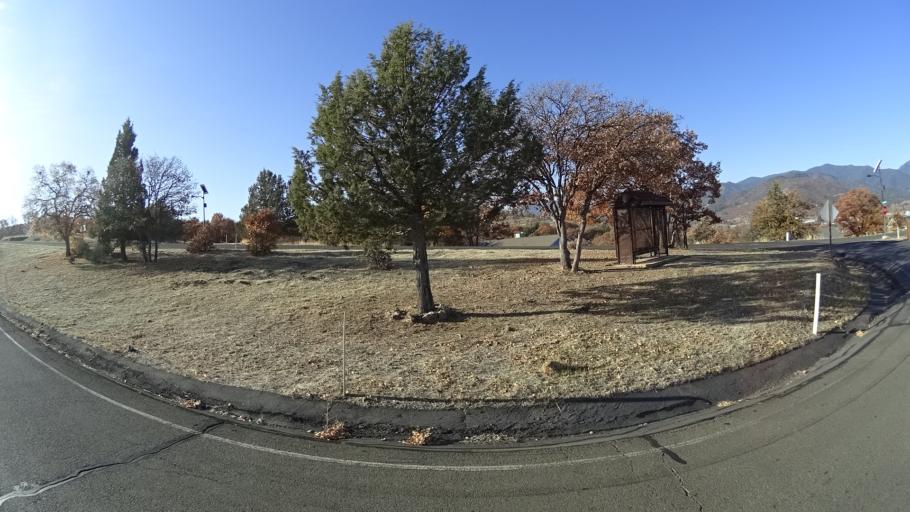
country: US
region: California
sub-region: Siskiyou County
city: Yreka
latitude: 41.7075
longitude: -122.6243
